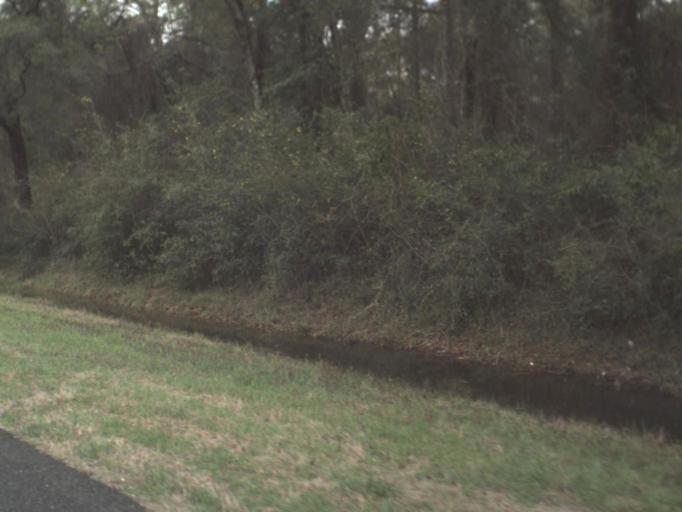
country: US
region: Florida
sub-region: Gadsden County
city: Havana
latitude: 30.5486
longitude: -84.3771
